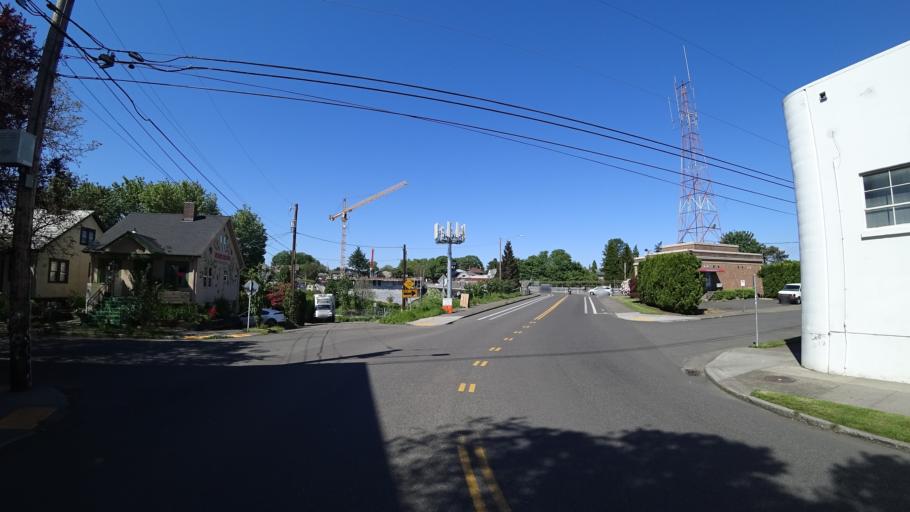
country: US
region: Oregon
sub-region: Multnomah County
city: Portland
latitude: 45.5292
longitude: -122.6455
